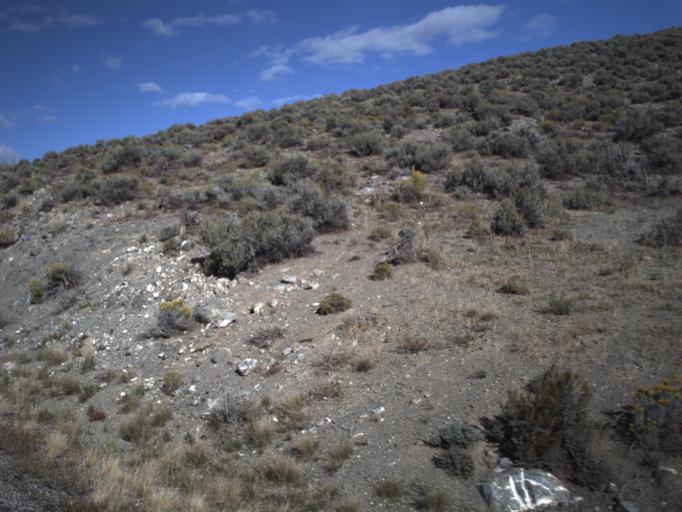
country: US
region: Utah
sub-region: Beaver County
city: Milford
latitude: 38.4241
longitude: -113.1127
